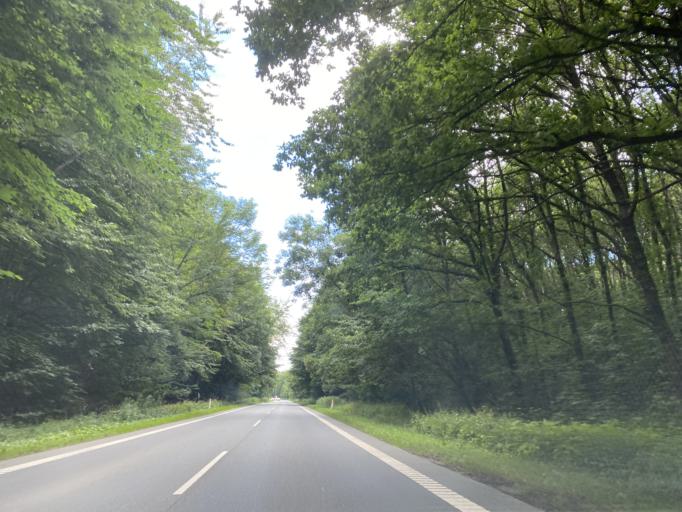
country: DK
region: Central Jutland
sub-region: Silkeborg Kommune
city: Silkeborg
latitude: 56.2591
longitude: 9.6250
